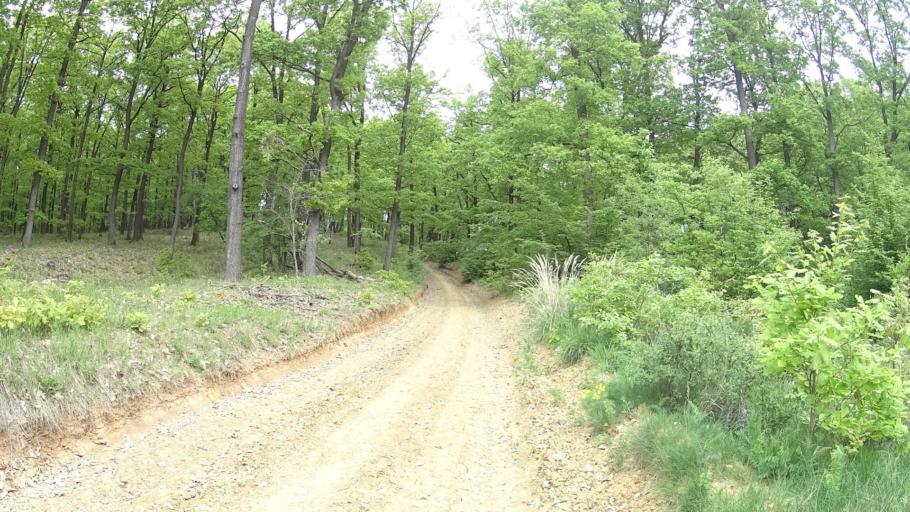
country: HU
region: Nograd
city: Romhany
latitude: 47.8905
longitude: 19.2472
